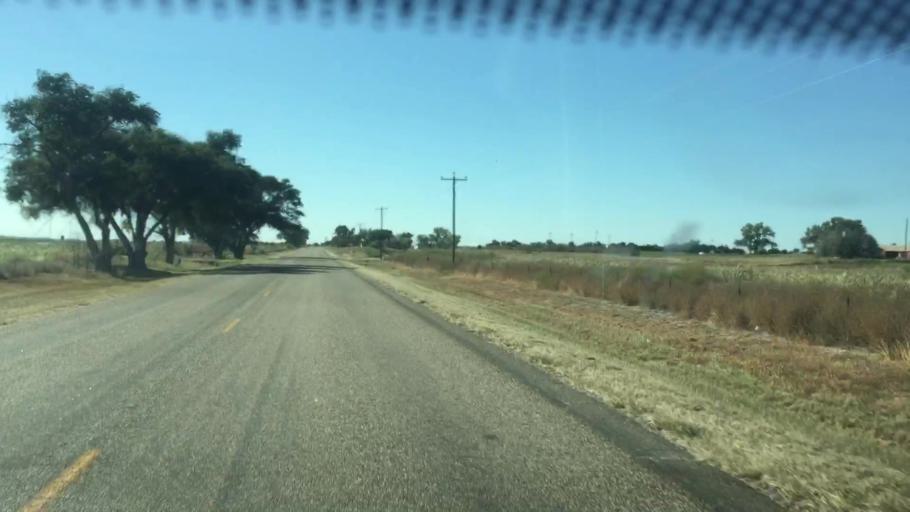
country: US
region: Colorado
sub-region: Prowers County
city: Lamar
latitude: 38.1150
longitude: -102.5831
